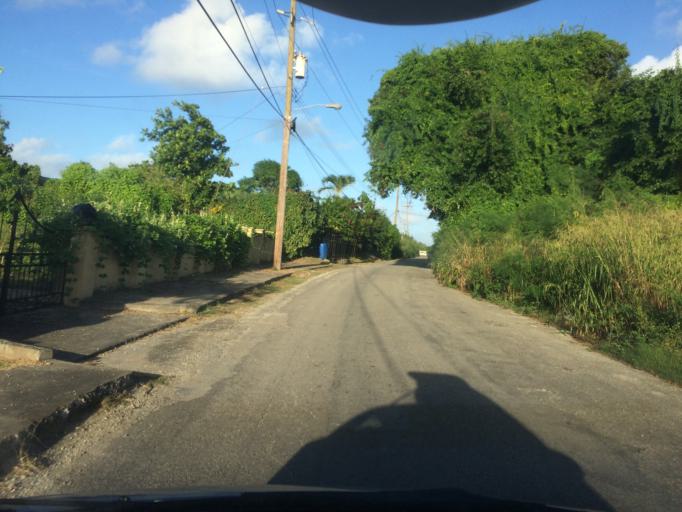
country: BB
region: Saint Lucy
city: Checker Hall
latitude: 13.3156
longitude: -59.6335
